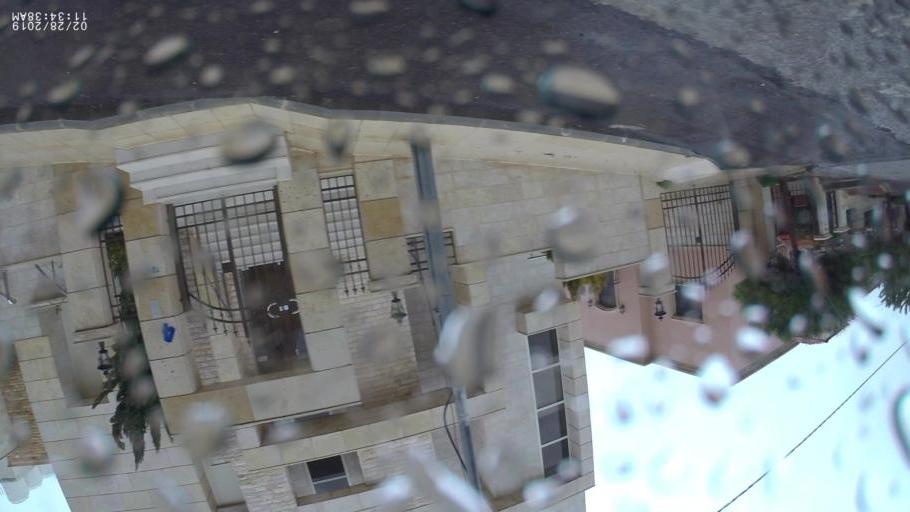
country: JO
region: Amman
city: Al Jubayhah
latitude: 32.0114
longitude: 35.8979
